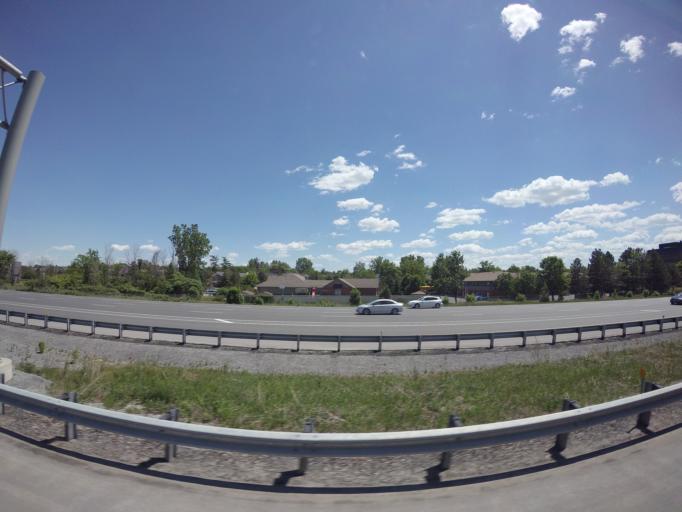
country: CA
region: Ontario
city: Bells Corners
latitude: 45.3166
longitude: -75.8931
